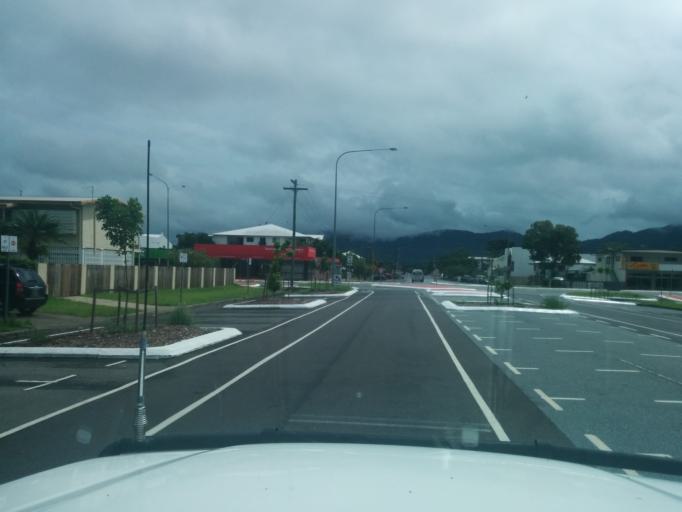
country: AU
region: Queensland
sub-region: Cairns
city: Cairns
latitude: -16.9191
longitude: 145.7689
